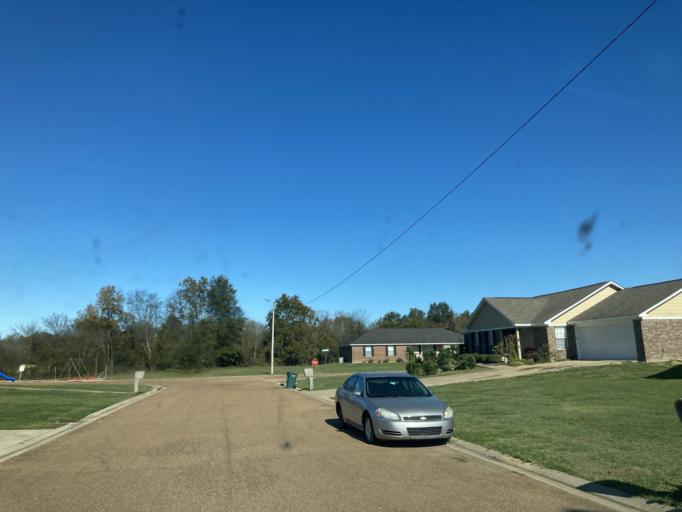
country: US
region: Mississippi
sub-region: Yazoo County
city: Yazoo City
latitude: 32.8586
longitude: -90.4266
